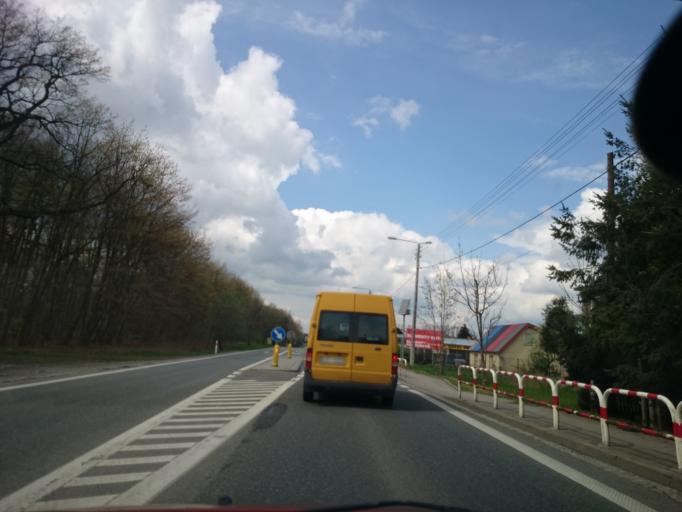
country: PL
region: Opole Voivodeship
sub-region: Powiat opolski
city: Tarnow Opolski
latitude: 50.5997
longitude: 18.0857
